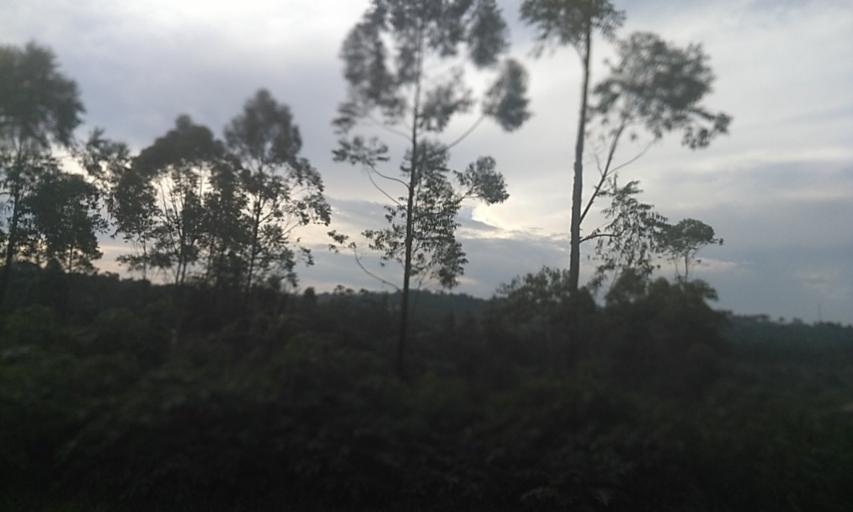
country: UG
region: Central Region
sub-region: Wakiso District
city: Kajansi
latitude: 0.2442
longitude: 32.4993
